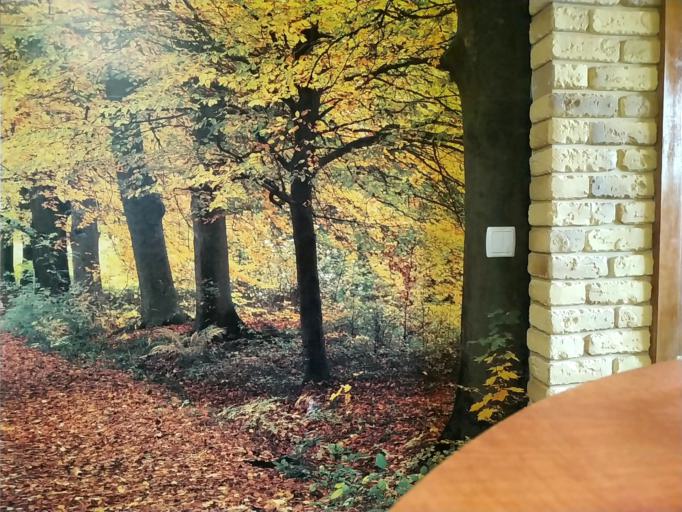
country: RU
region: Novgorod
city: Opechenskiy Posad
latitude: 58.2660
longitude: 34.0319
